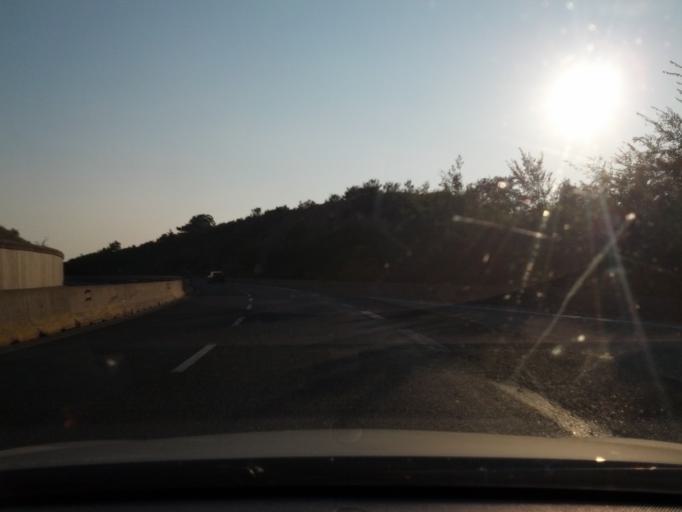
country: IT
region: Friuli Venezia Giulia
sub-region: Provincia di Trieste
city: Trieste
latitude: 45.6373
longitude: 13.8143
